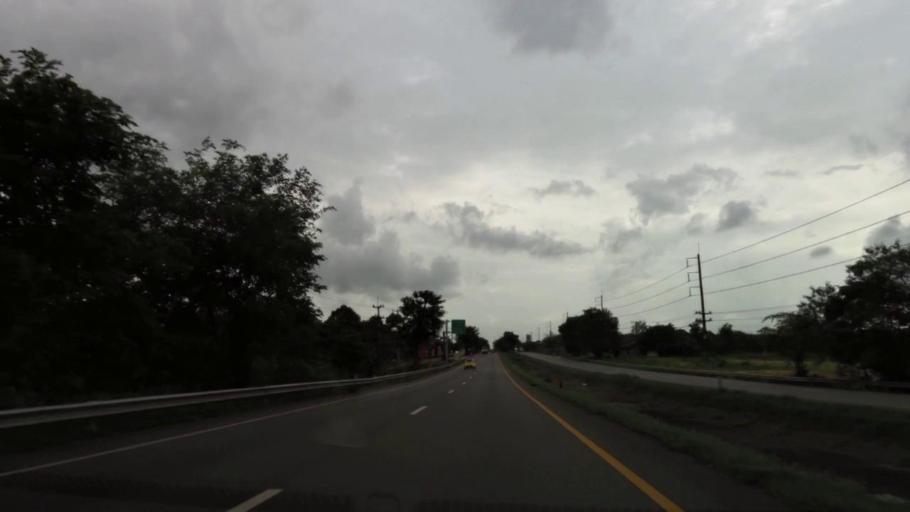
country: TH
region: Chanthaburi
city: Tha Mai
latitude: 12.7066
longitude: 101.9836
